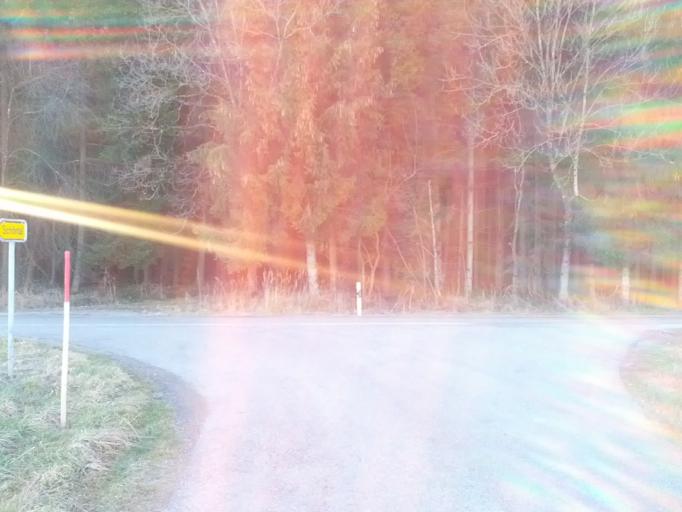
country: DE
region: Baden-Wuerttemberg
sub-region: Tuebingen Region
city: Rot an der Rot
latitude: 47.9765
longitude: 10.0056
